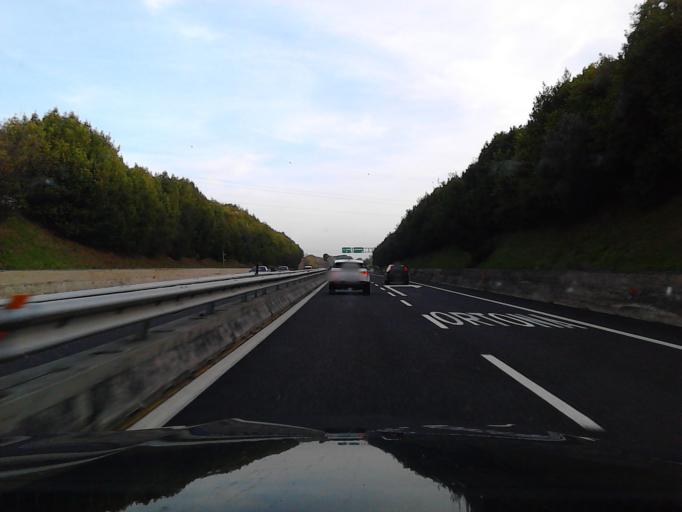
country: IT
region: Abruzzo
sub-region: Provincia di Chieti
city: Ortona
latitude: 42.3329
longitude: 14.3747
